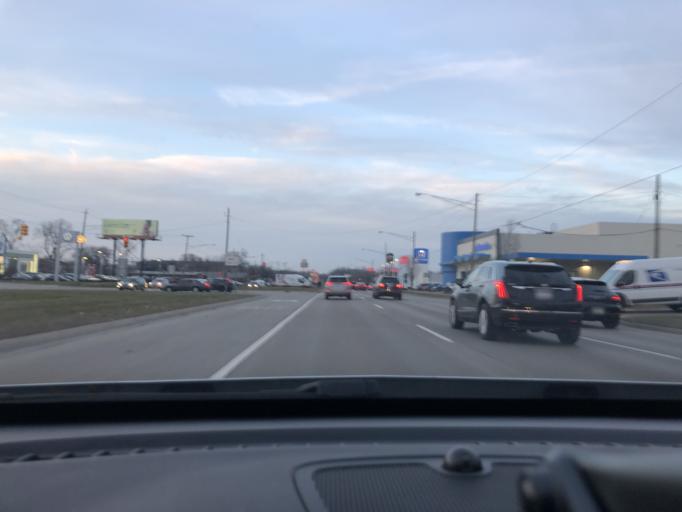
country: US
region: Michigan
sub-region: Wayne County
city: Inkster
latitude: 42.2943
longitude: -83.2712
